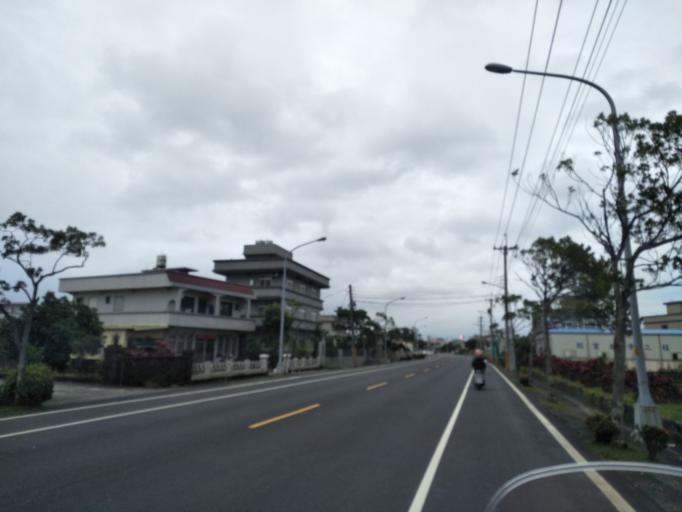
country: TW
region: Taiwan
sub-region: Yilan
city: Yilan
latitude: 24.7771
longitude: 121.7830
